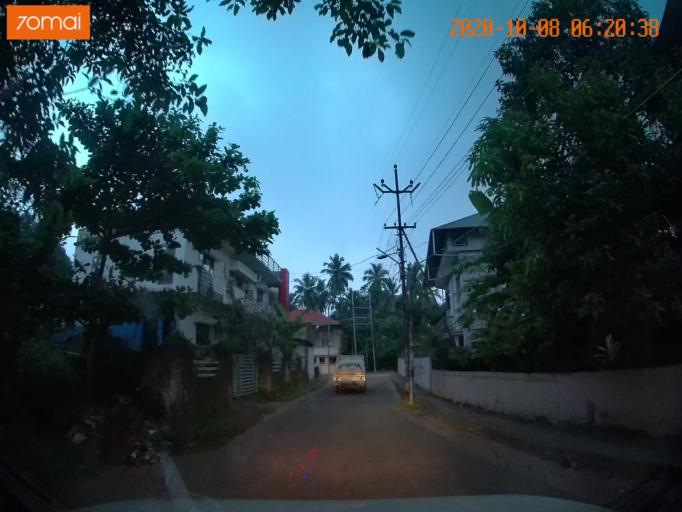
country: IN
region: Kerala
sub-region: Thrissur District
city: Trichur
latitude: 10.5193
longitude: 76.2356
